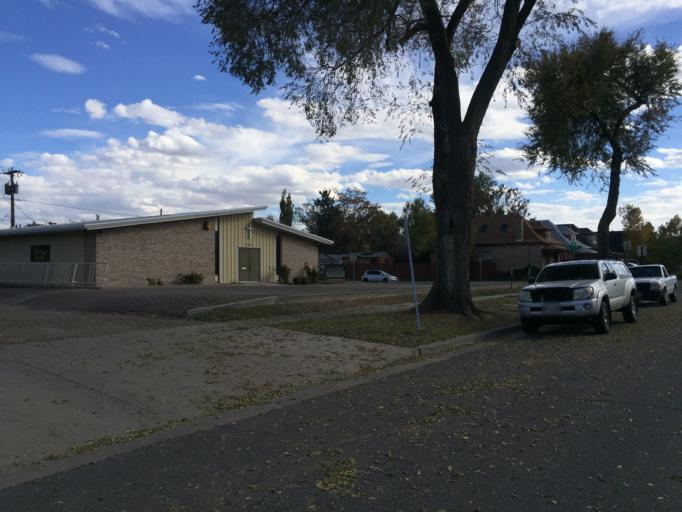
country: US
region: Colorado
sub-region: Denver County
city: Denver
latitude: 39.7625
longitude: -104.9647
